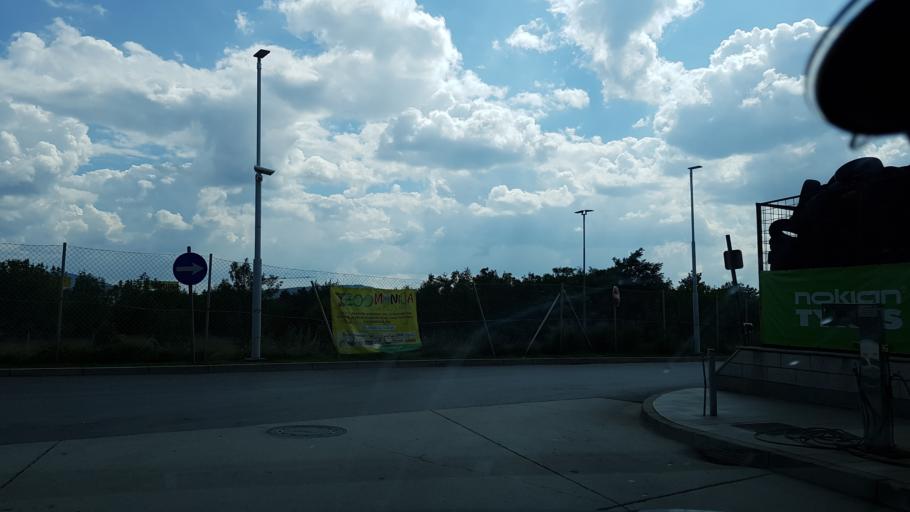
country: SI
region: Sezana
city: Sezana
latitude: 45.7026
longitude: 13.8437
